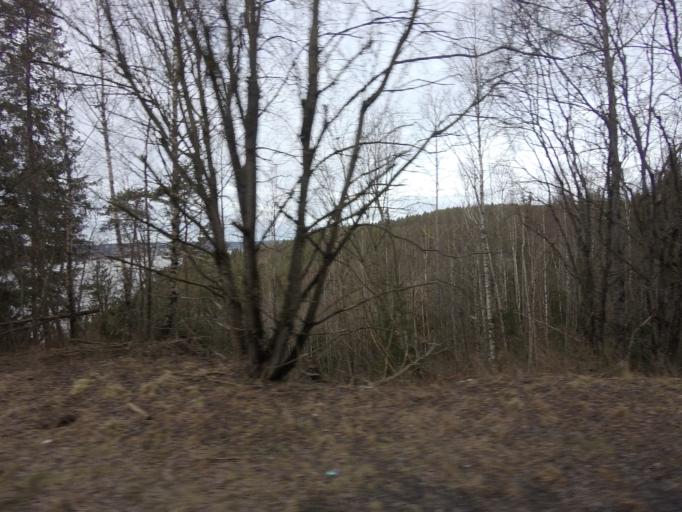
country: NO
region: Akershus
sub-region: Enebakk
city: Flateby
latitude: 59.8267
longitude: 11.2424
